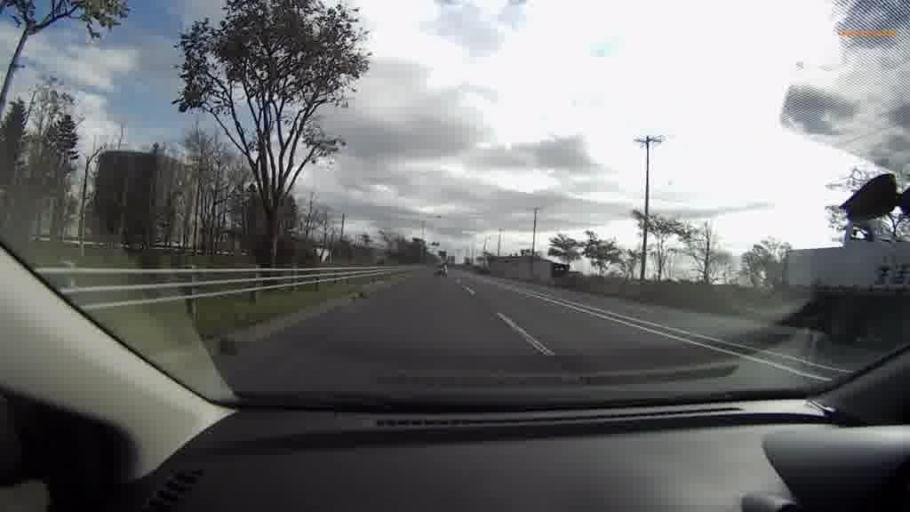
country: JP
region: Hokkaido
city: Kushiro
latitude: 43.0099
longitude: 144.2788
